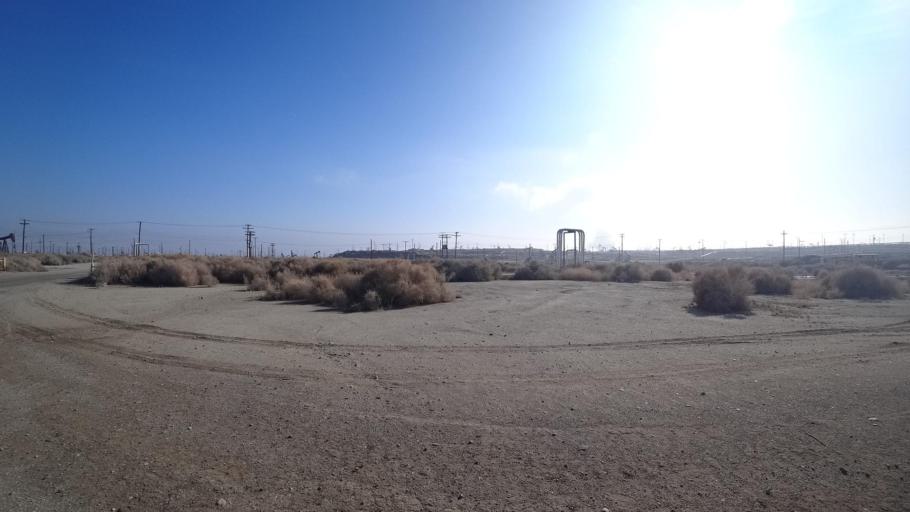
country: US
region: California
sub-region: Kern County
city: Taft Heights
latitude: 35.2223
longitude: -119.5961
